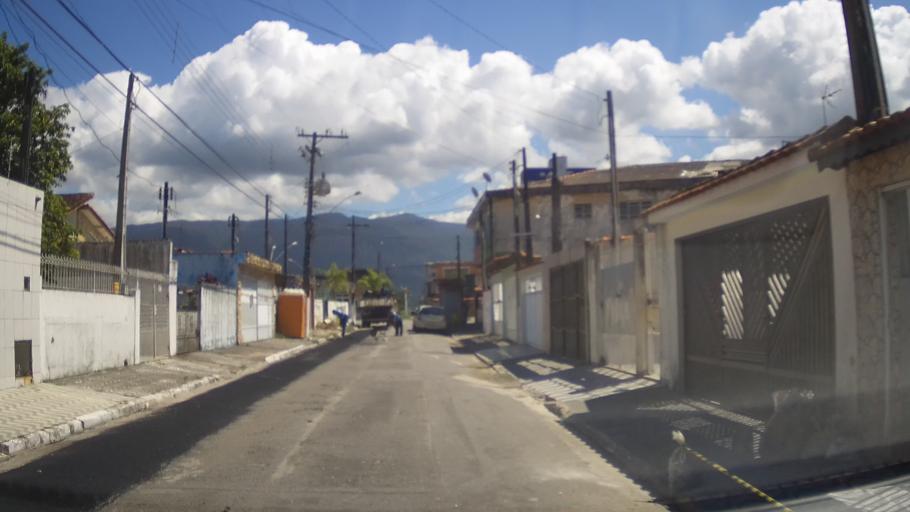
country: BR
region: Sao Paulo
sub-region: Mongagua
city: Mongagua
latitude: -24.0462
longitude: -46.5264
